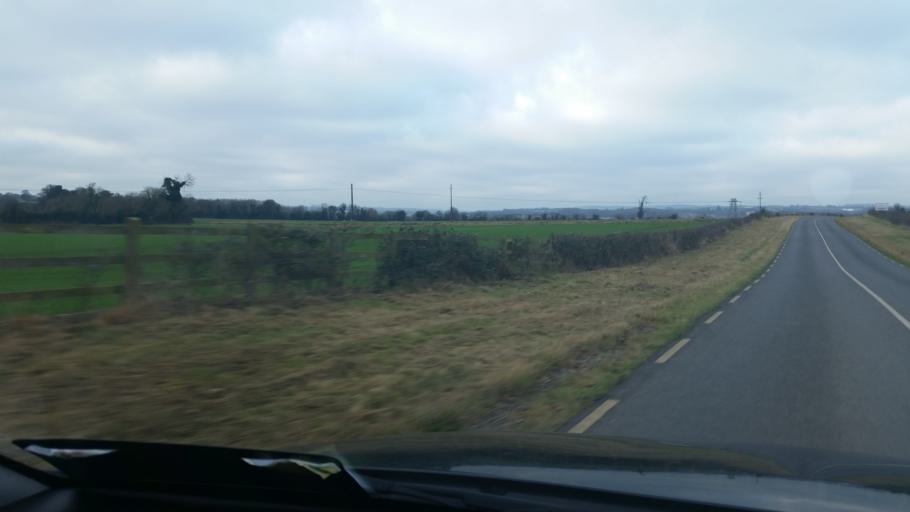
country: IE
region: Leinster
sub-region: Lu
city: Tullyallen
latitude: 53.7095
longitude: -6.4112
